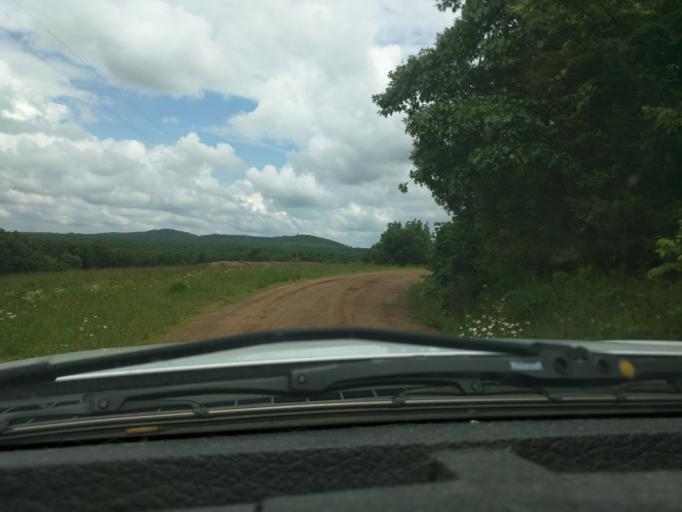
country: US
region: Arkansas
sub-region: Madison County
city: Huntsville
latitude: 35.8838
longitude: -93.5412
